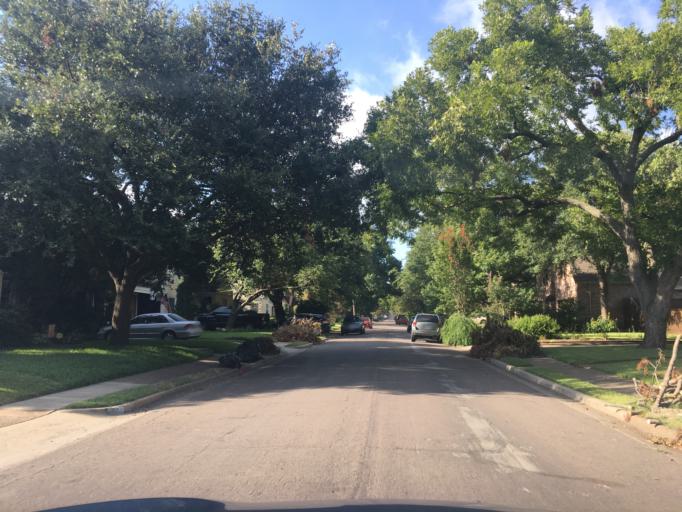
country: US
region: Texas
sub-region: Dallas County
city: Highland Park
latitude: 32.8398
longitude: -96.7625
